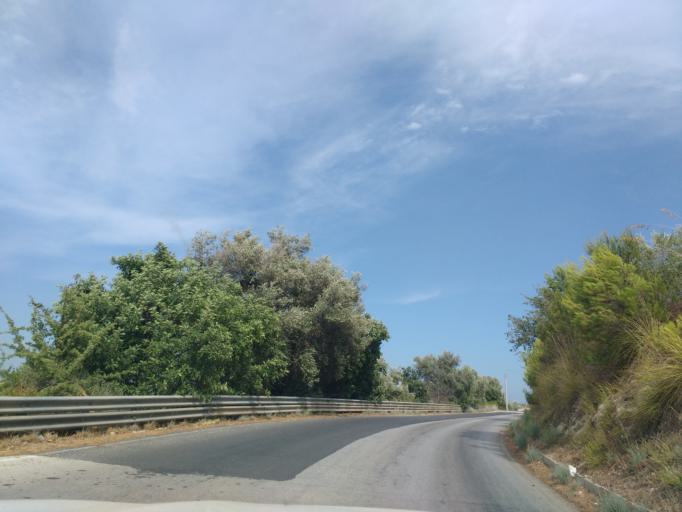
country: IT
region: Sicily
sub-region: Provincia di Siracusa
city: Noto
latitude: 36.8798
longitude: 15.0679
